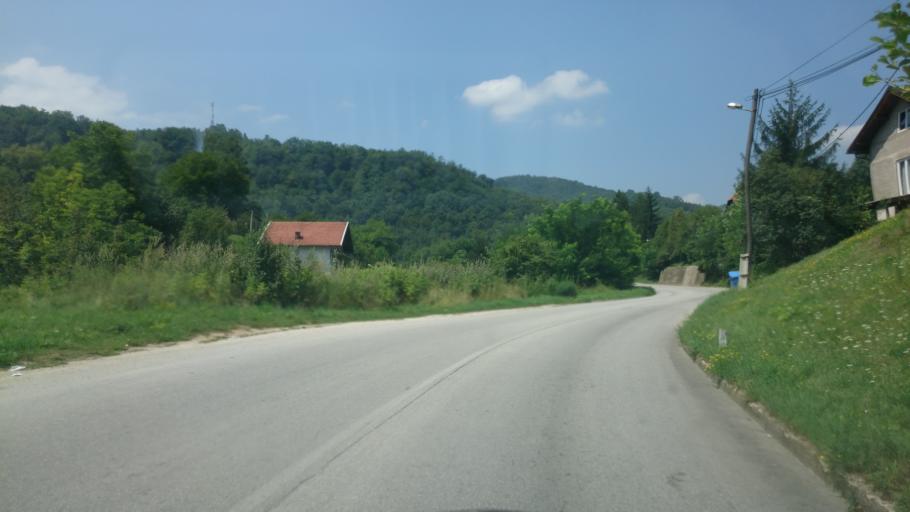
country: BA
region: Federation of Bosnia and Herzegovina
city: Lokvine
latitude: 44.1881
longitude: 17.8629
